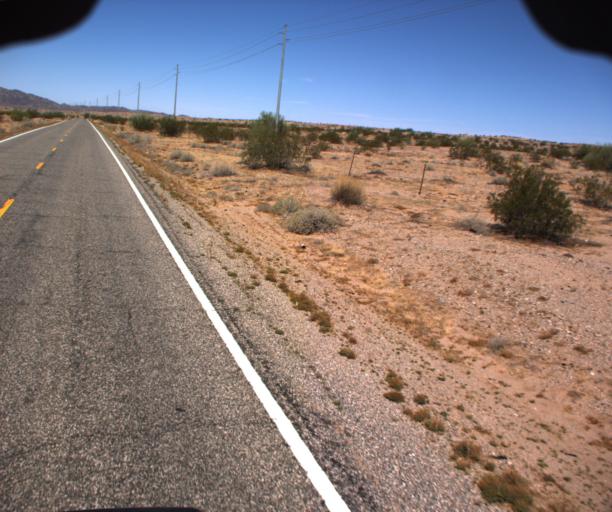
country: US
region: Arizona
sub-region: La Paz County
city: Parker
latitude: 33.9953
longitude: -114.1783
